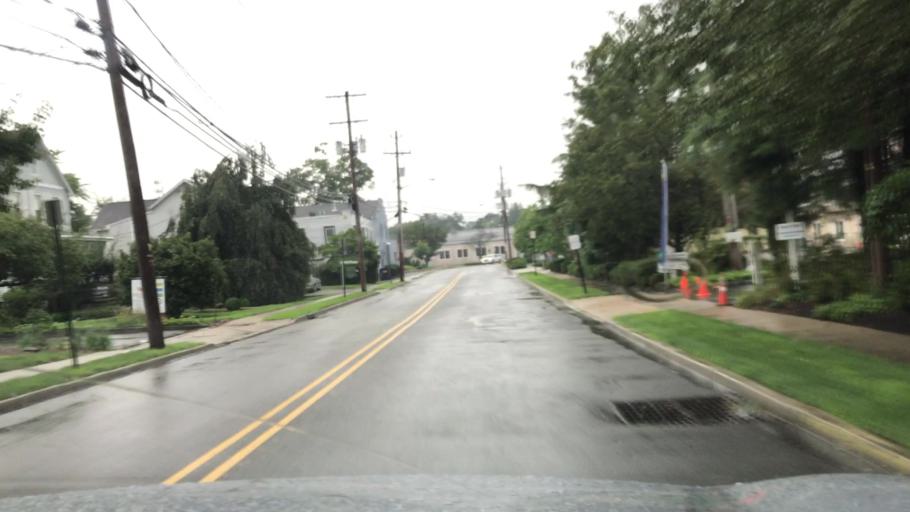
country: US
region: New Jersey
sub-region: Bergen County
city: Closter
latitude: 40.9752
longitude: -73.9598
